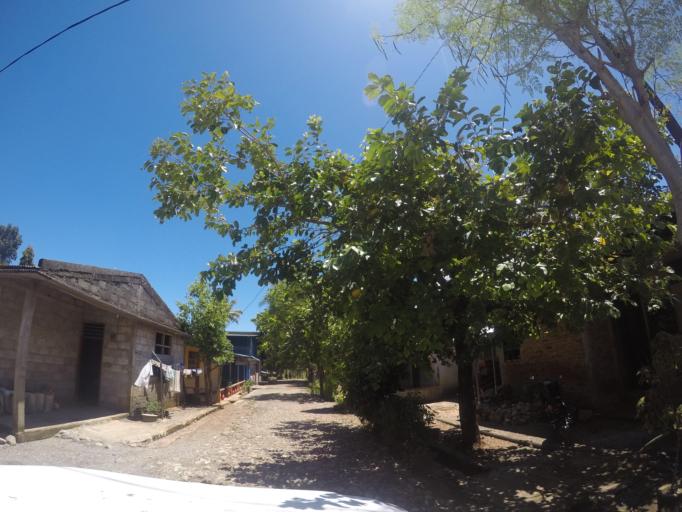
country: TL
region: Bobonaro
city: Maliana
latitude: -8.9716
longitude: 125.2167
